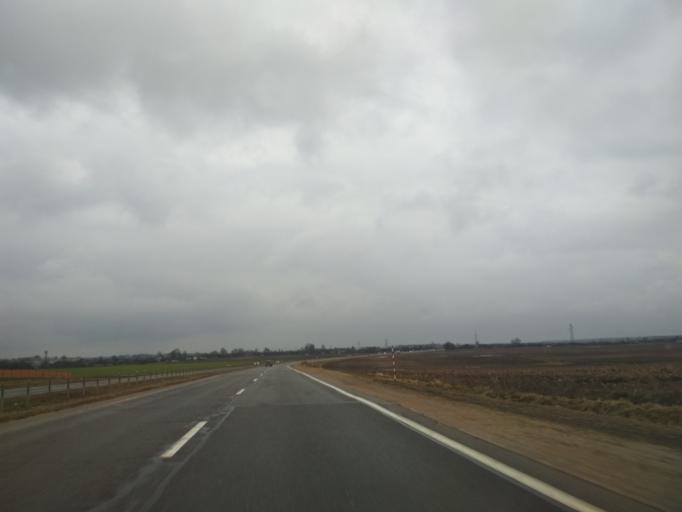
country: BY
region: Minsk
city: Dukora
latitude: 53.6787
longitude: 27.9256
